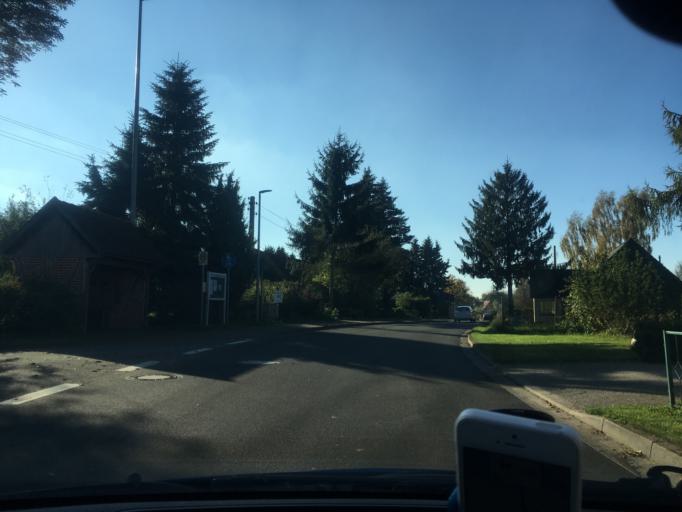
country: DE
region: Mecklenburg-Vorpommern
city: Dummer
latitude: 53.5686
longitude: 11.2269
